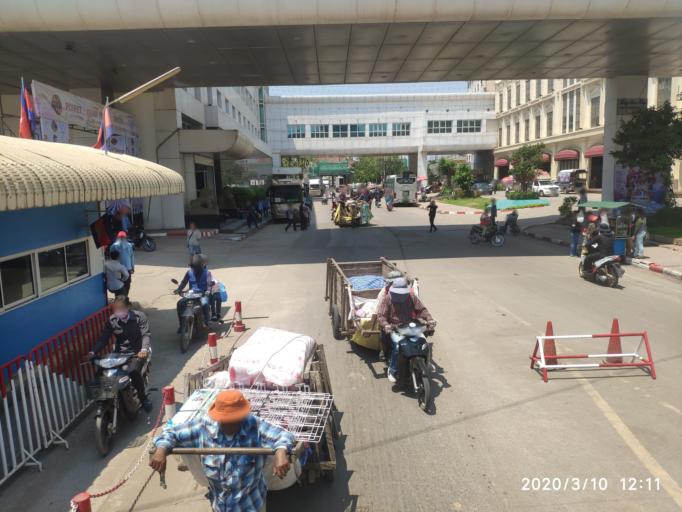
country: KH
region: Banteay Meanchey
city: Paoy Pet
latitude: 13.6601
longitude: 102.5521
